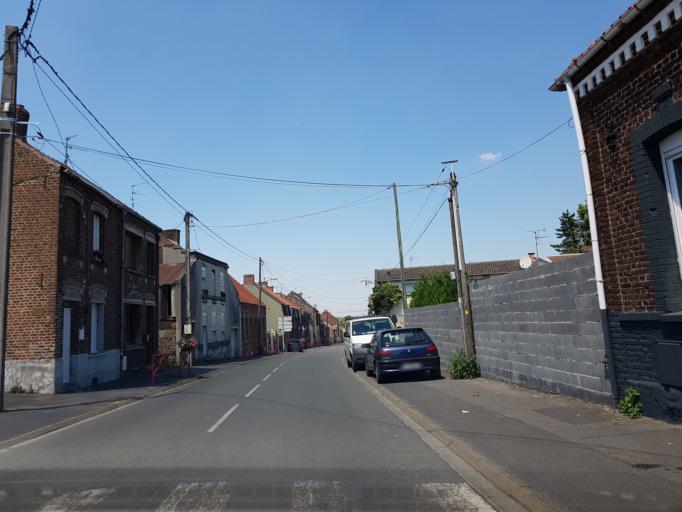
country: FR
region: Nord-Pas-de-Calais
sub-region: Departement du Nord
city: Neuville-sur-Escaut
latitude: 50.2982
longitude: 3.3568
